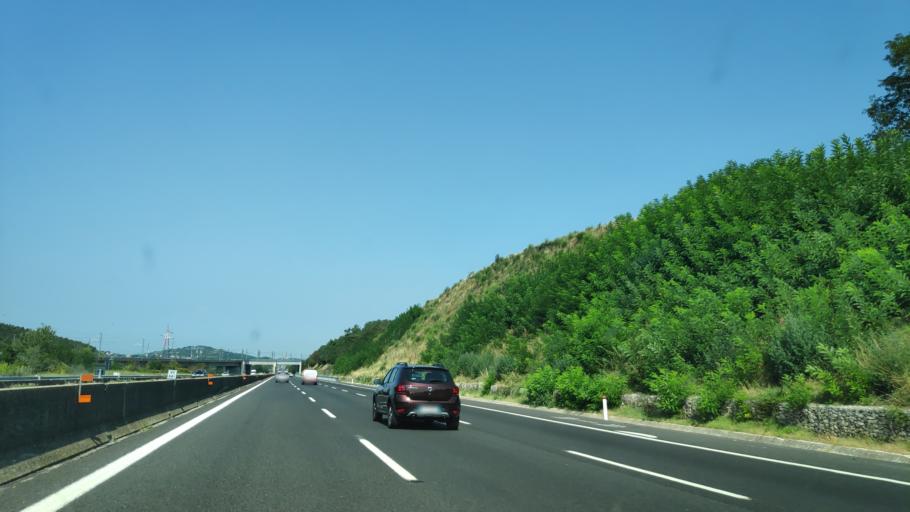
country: IT
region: Campania
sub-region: Provincia di Caserta
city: Bivio Mortola
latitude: 41.4212
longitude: 13.9276
